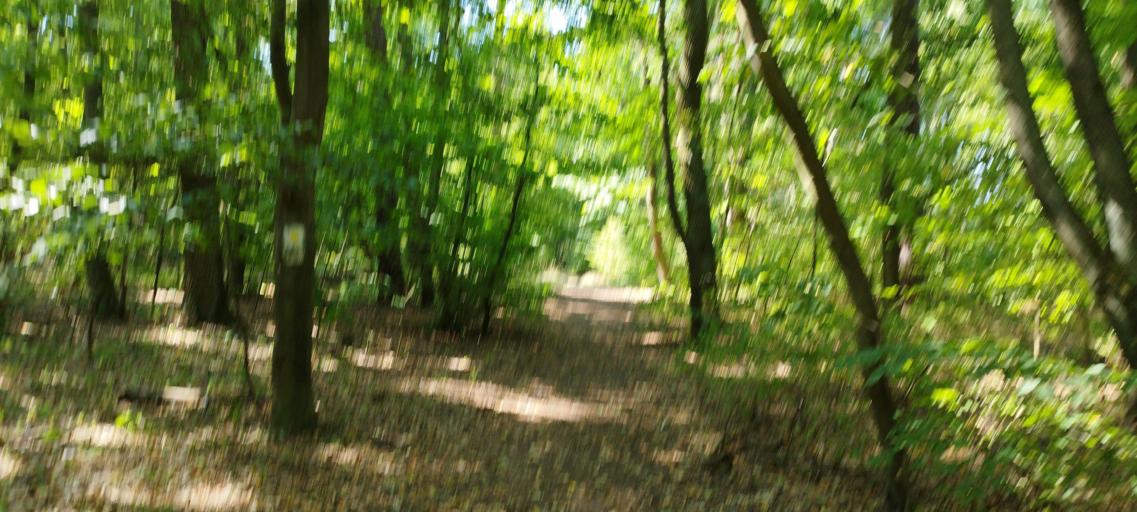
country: DE
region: Brandenburg
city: Rehfelde
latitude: 52.5306
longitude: 13.8462
